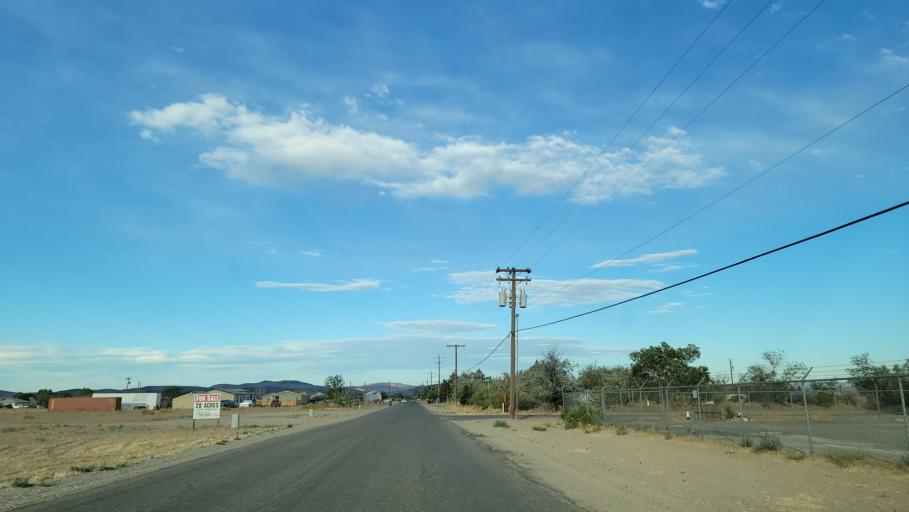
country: US
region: Nevada
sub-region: Lyon County
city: Silver Springs
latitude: 39.4007
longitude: -119.2351
